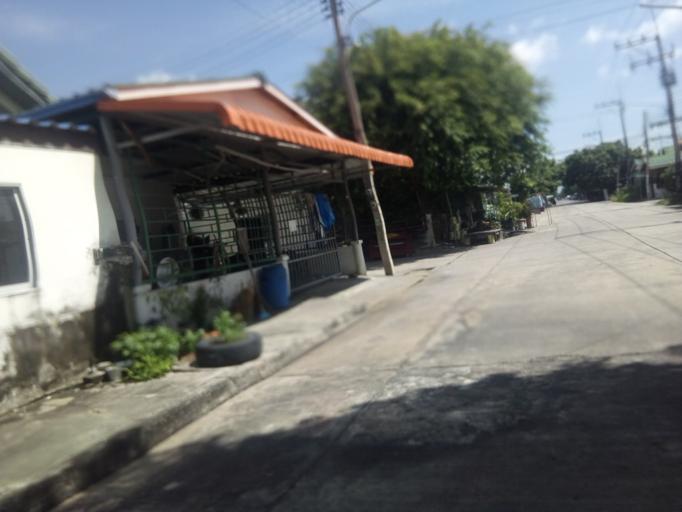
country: TH
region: Pathum Thani
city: Nong Suea
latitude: 14.0481
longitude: 100.8516
